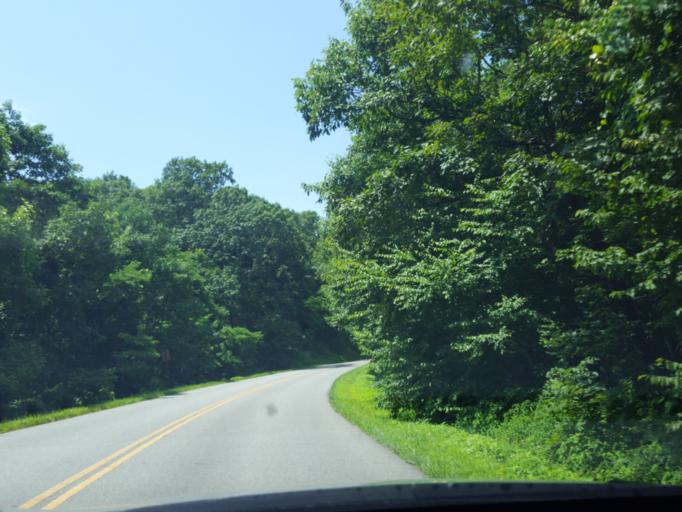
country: US
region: Virginia
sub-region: Nelson County
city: Nellysford
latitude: 37.9413
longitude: -78.9372
